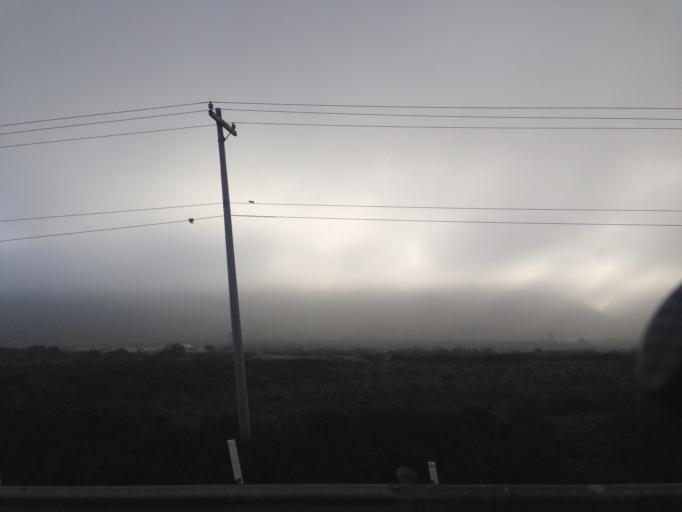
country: MX
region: Baja California
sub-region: Playas de Rosarito
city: Santa Anita
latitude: 32.0630
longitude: -116.8774
